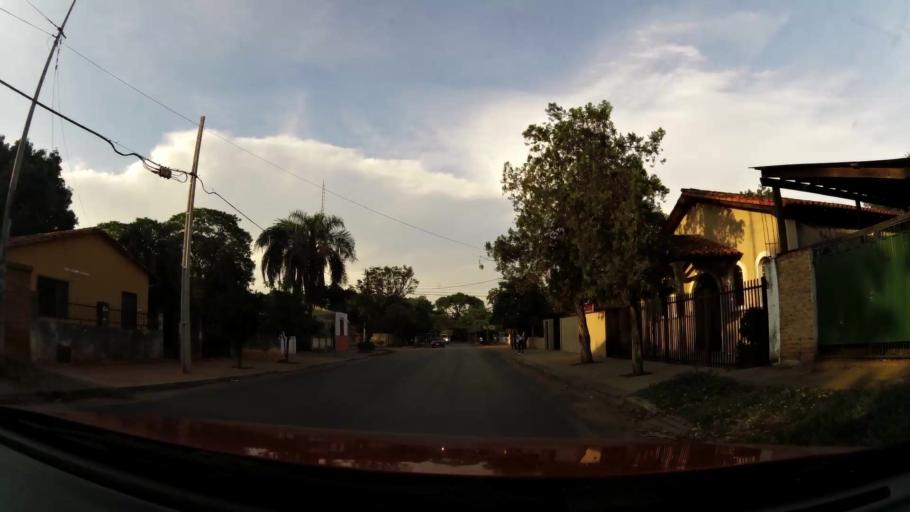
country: PY
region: Central
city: San Lorenzo
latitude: -25.3567
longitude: -57.5055
